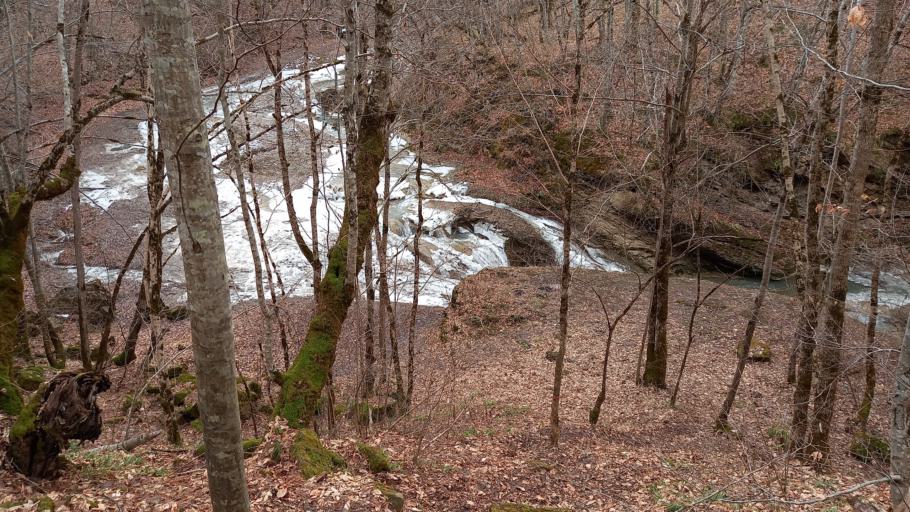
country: RU
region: Adygeya
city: Kamennomostskiy
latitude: 44.1745
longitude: 40.3000
